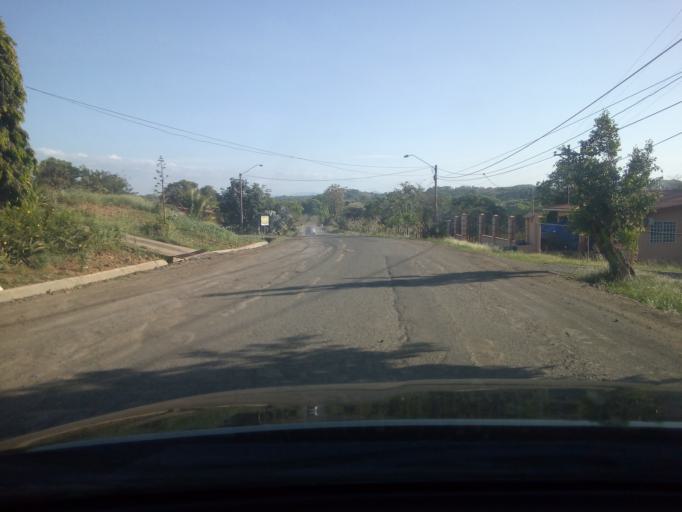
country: PA
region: Veraguas
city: Atalaya
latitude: 8.0441
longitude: -80.9321
